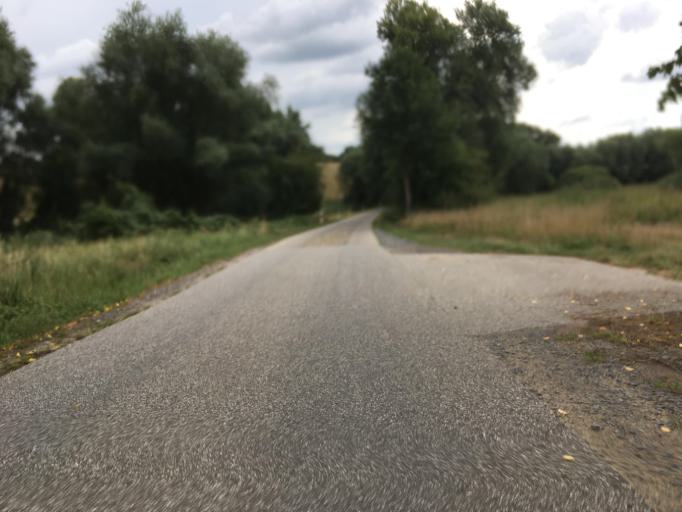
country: DE
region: Brandenburg
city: Prenzlau
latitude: 53.2396
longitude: 13.8782
